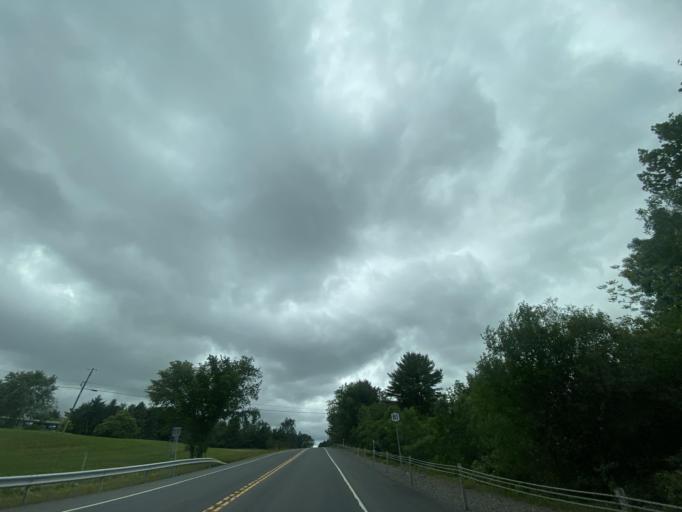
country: US
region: New York
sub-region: Greene County
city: Cairo
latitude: 42.3946
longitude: -73.9758
